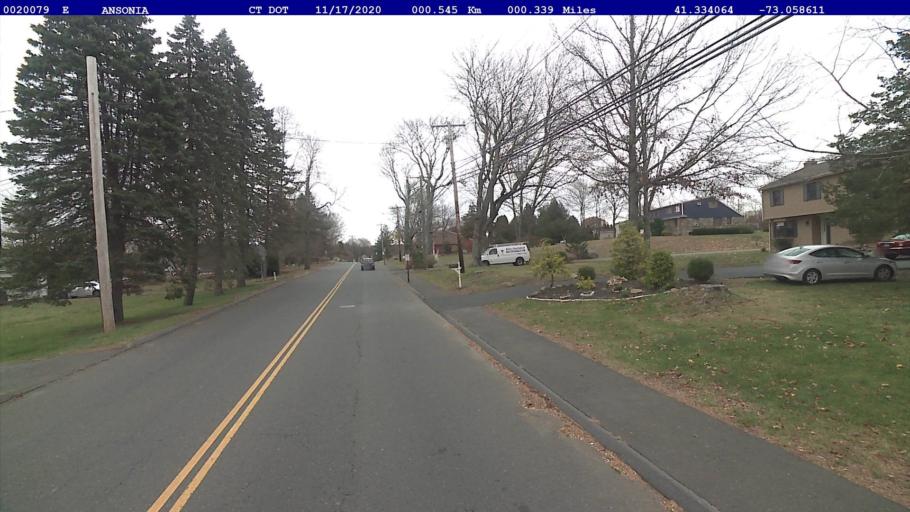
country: US
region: Connecticut
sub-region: New Haven County
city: Ansonia
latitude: 41.3341
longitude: -73.0586
